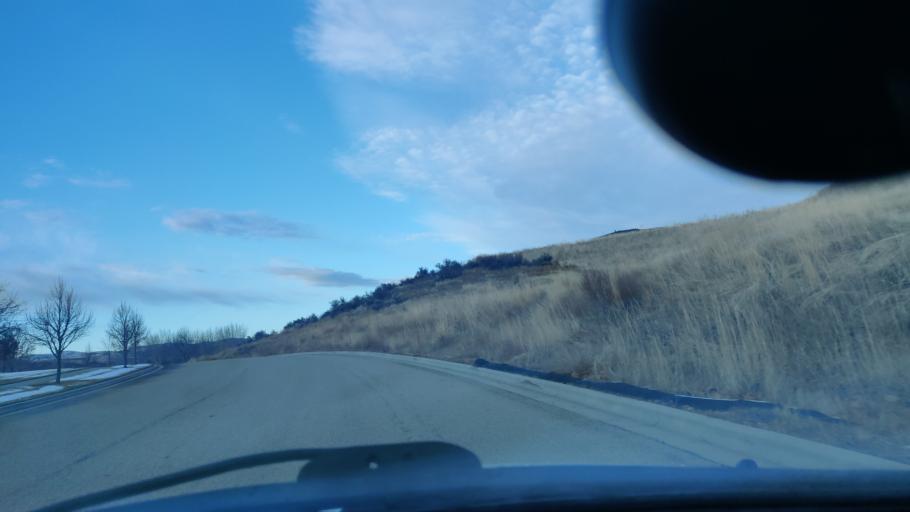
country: US
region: Idaho
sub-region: Ada County
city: Eagle
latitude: 43.7753
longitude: -116.2609
